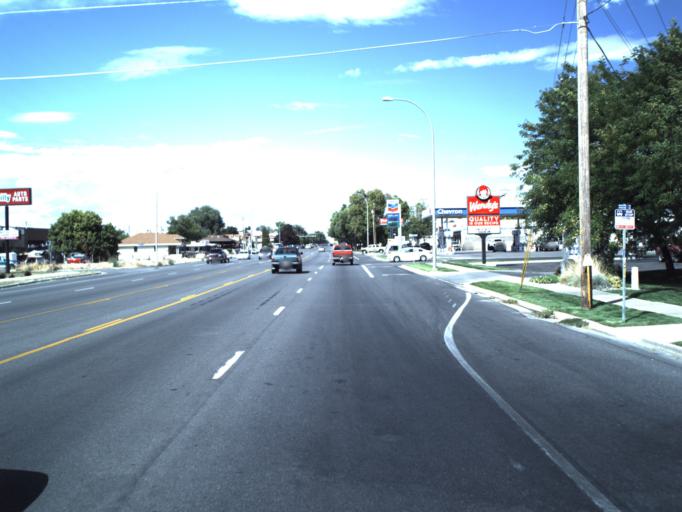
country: US
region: Utah
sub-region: Cache County
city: Smithfield
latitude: 41.8194
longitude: -111.8330
